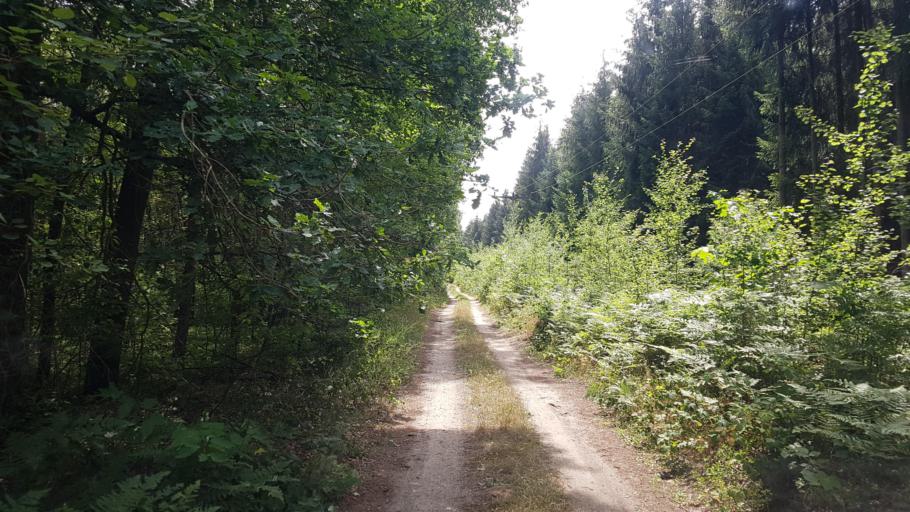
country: DE
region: Brandenburg
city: Sallgast
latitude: 51.5951
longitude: 13.9023
